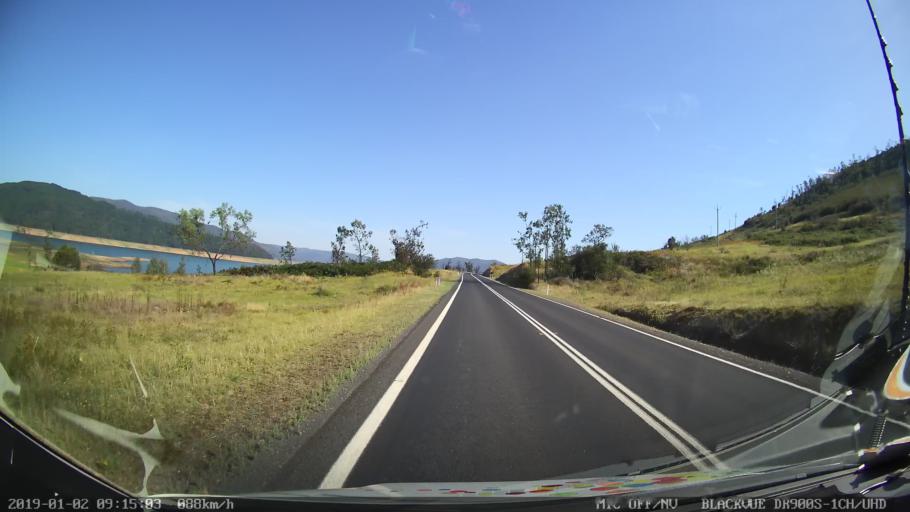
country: AU
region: New South Wales
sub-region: Tumut Shire
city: Tumut
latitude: -35.4698
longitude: 148.2788
